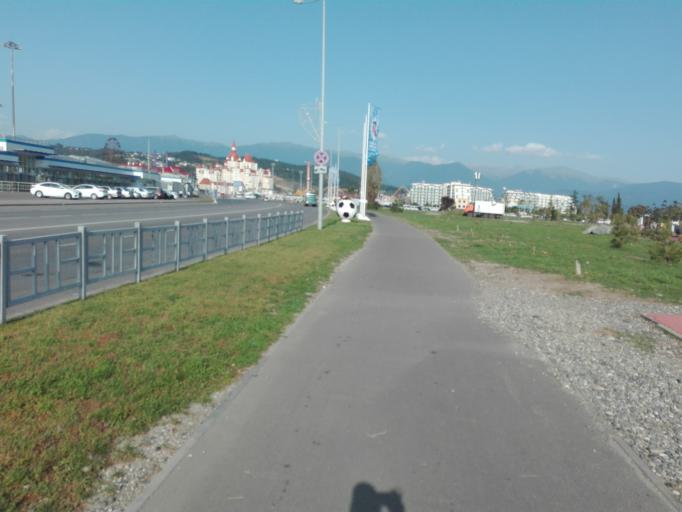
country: RU
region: Krasnodarskiy
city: Adler
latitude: 43.3996
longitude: 39.9561
